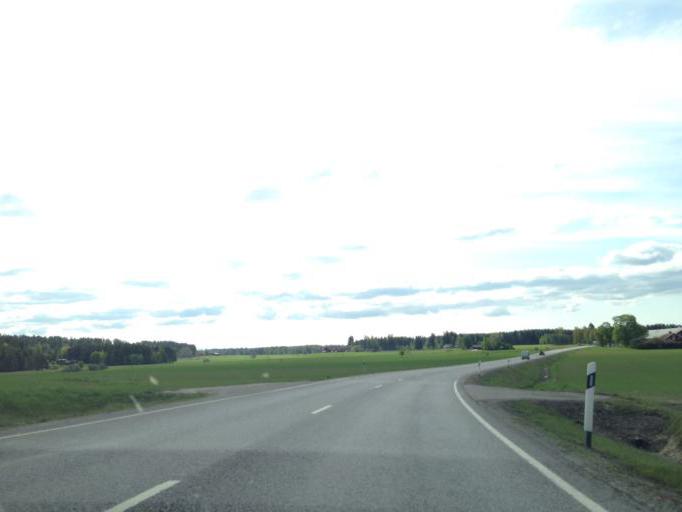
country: SE
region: Soedermanland
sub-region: Nykopings Kommun
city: Svalsta
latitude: 58.8631
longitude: 16.9116
